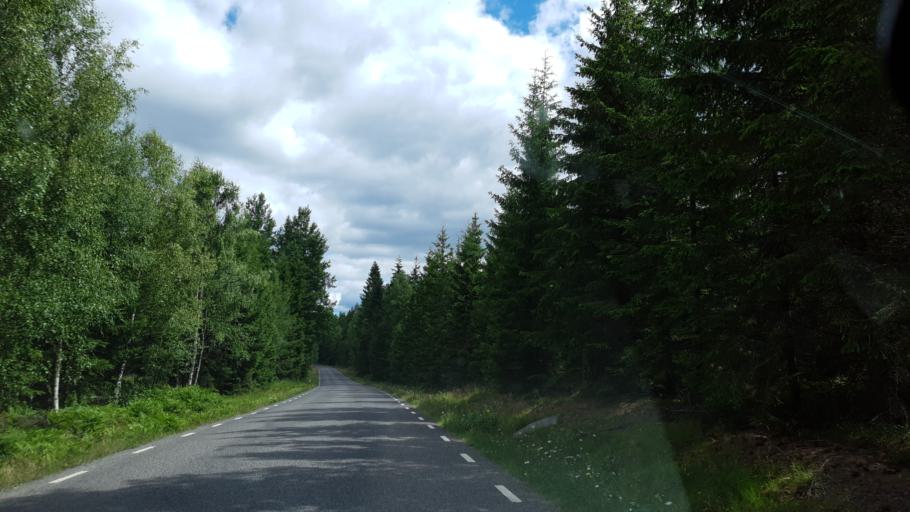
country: SE
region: Kronoberg
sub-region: Uppvidinge Kommun
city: Aseda
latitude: 57.1883
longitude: 15.3883
